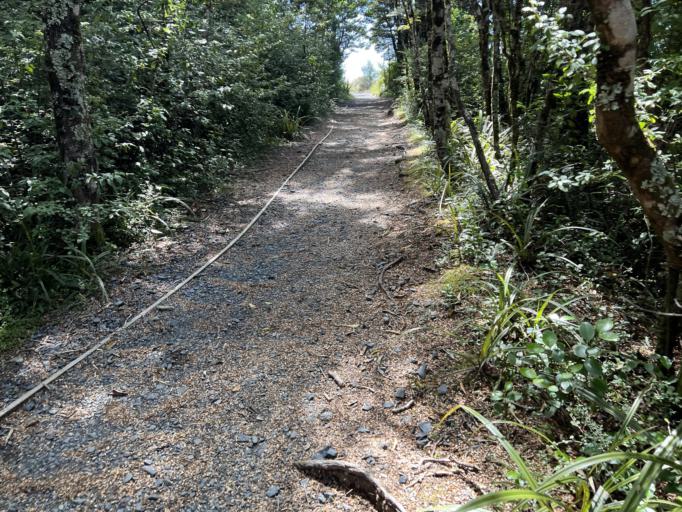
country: NZ
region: Manawatu-Wanganui
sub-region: Ruapehu District
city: Waiouru
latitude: -39.2007
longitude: 175.5478
